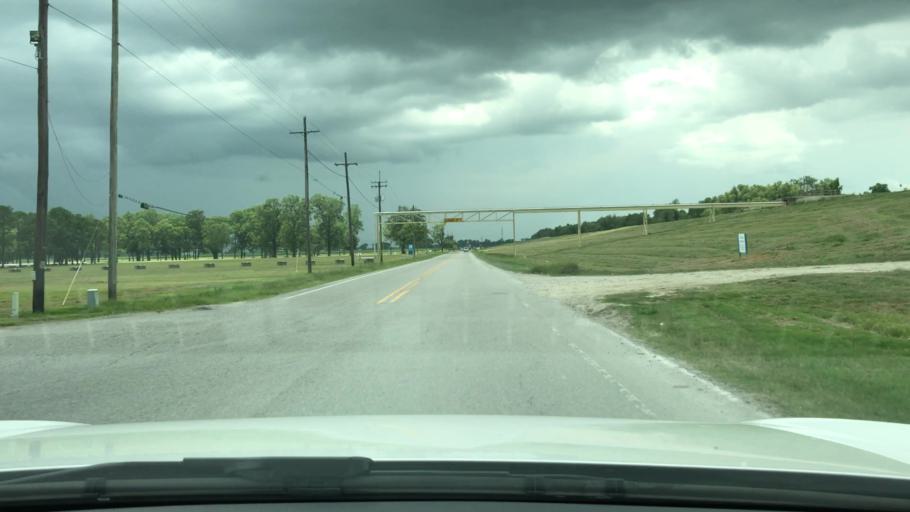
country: US
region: Louisiana
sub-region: Iberville Parish
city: Plaquemine
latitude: 30.2732
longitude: -91.1817
